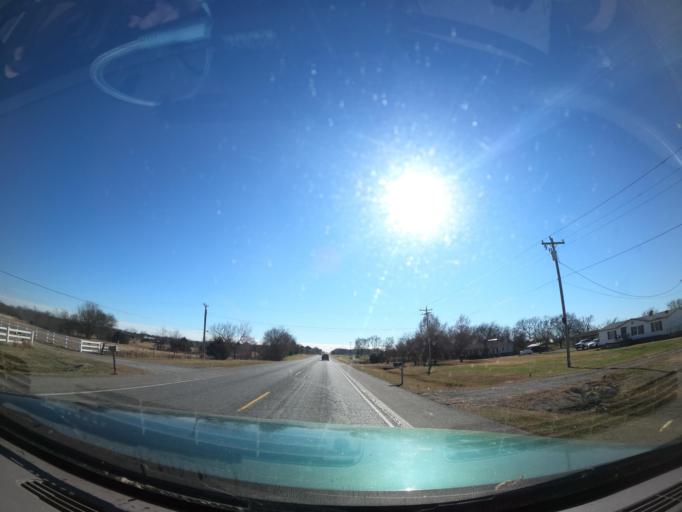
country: US
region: Oklahoma
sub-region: Muskogee County
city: Haskell
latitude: 35.8514
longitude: -95.6775
